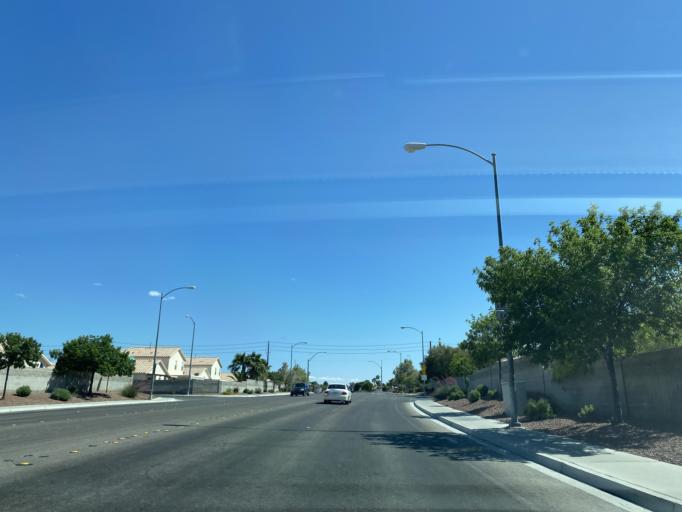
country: US
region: Nevada
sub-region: Clark County
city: Spring Valley
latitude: 36.0876
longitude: -115.2165
